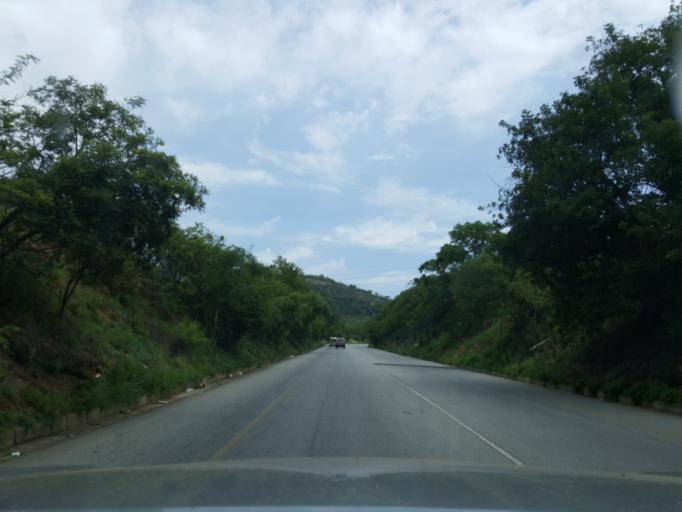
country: ZA
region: Mpumalanga
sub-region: Ehlanzeni District
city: Nelspruit
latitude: -25.4642
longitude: 31.0927
